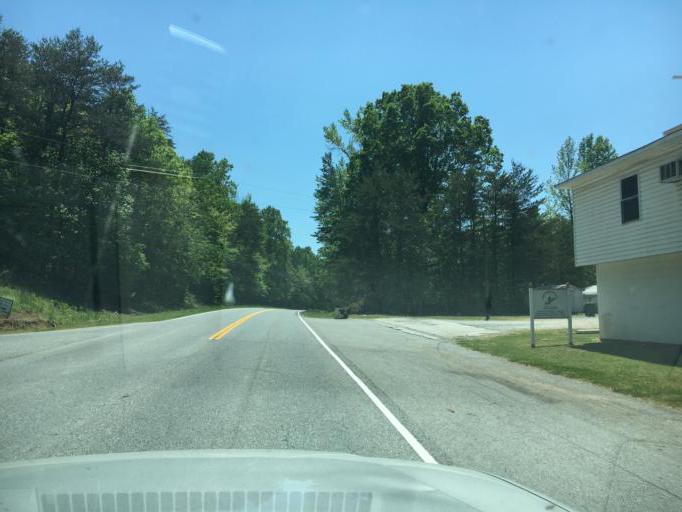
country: US
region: South Carolina
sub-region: Cherokee County
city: Blacksburg
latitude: 35.1304
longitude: -81.5832
